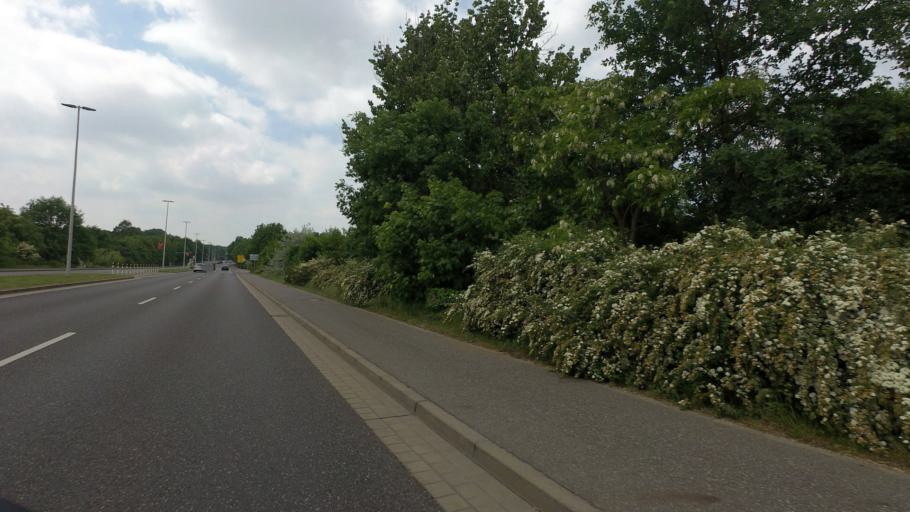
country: DE
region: Brandenburg
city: Cottbus
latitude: 51.7552
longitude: 14.3561
